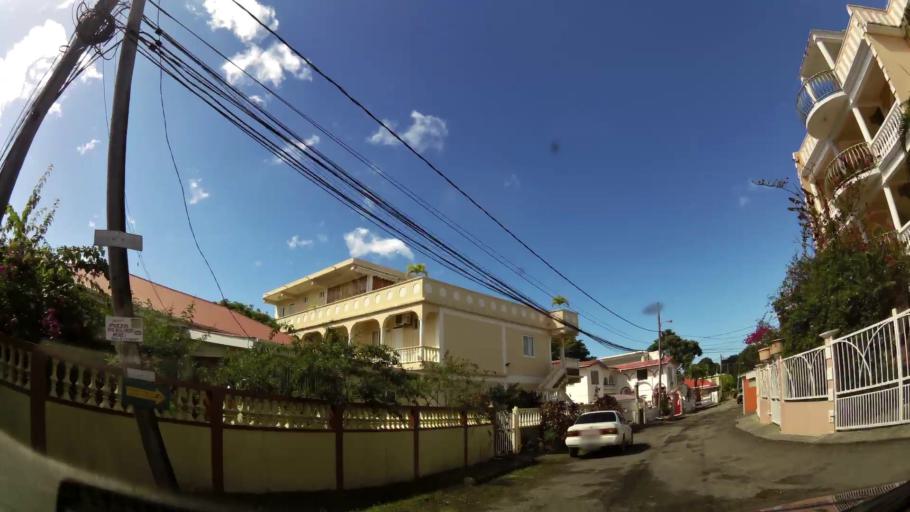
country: DM
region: Saint John
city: Portsmouth
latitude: 15.5592
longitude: -61.4572
